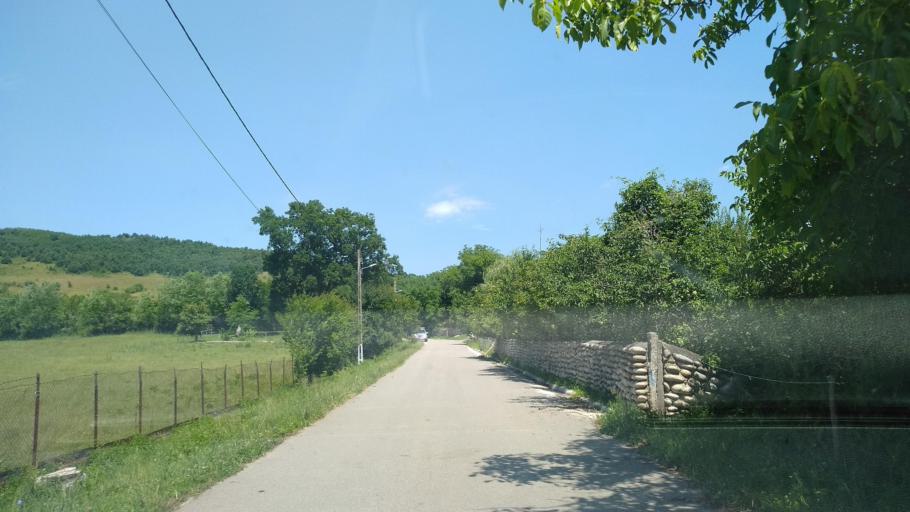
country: RO
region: Hunedoara
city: Densus
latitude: 45.5811
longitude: 22.8047
